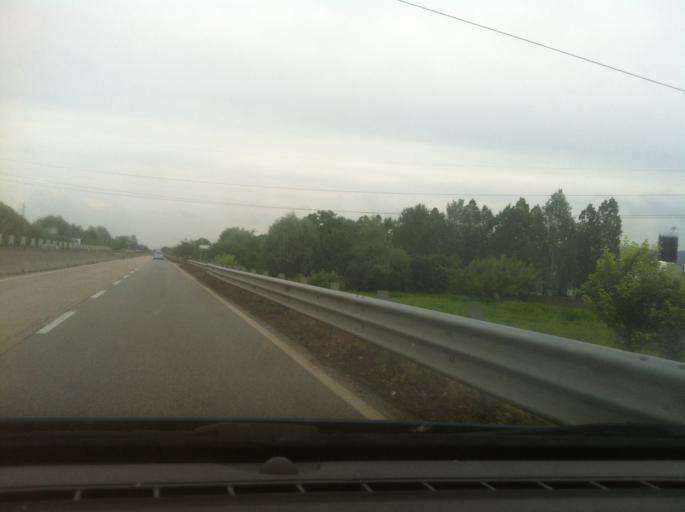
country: IT
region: Piedmont
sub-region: Provincia di Torino
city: Settimo Torinese
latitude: 45.1334
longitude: 7.7867
